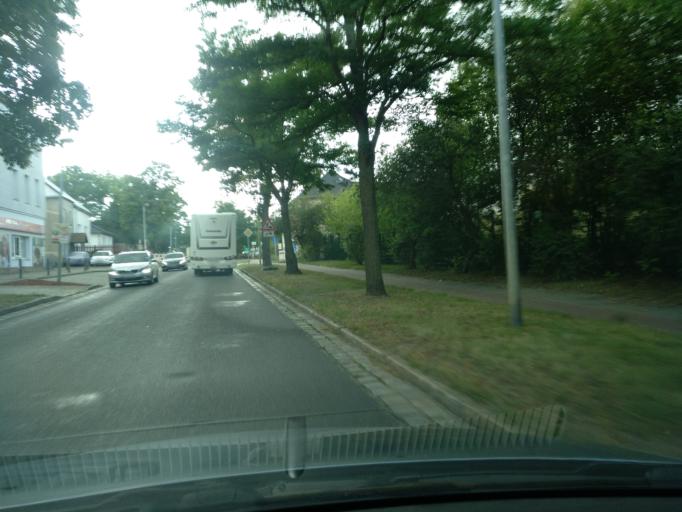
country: DE
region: Brandenburg
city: Woltersdorf
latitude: 52.4836
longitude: 13.7774
